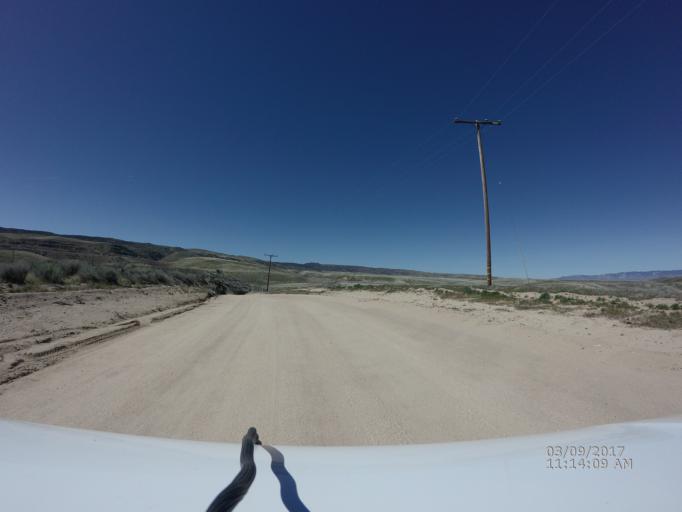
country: US
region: California
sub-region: Los Angeles County
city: Green Valley
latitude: 34.7029
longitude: -118.3925
